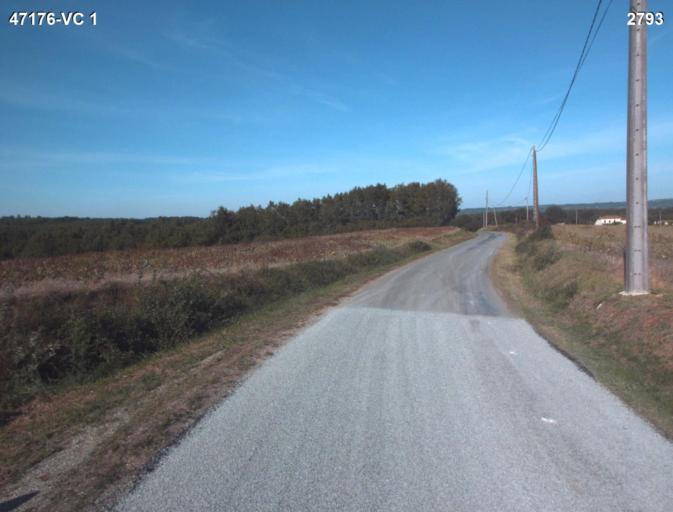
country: FR
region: Aquitaine
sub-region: Departement du Lot-et-Garonne
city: Vianne
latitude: 44.2160
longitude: 0.3011
